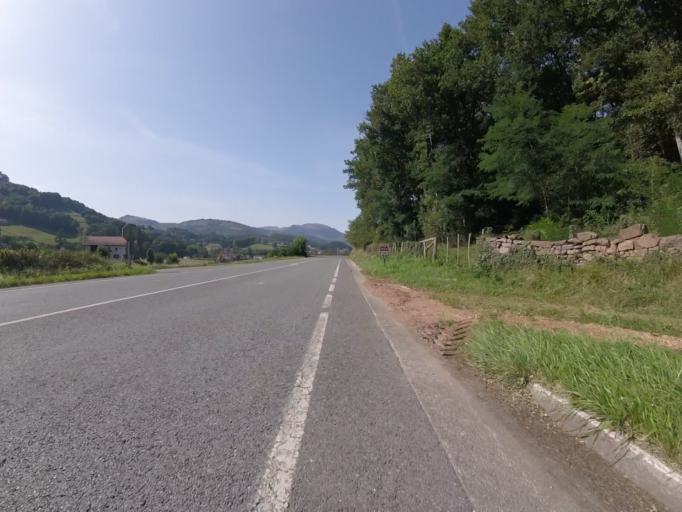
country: ES
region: Navarre
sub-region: Provincia de Navarra
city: Zugarramurdi
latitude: 43.1533
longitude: -1.5043
